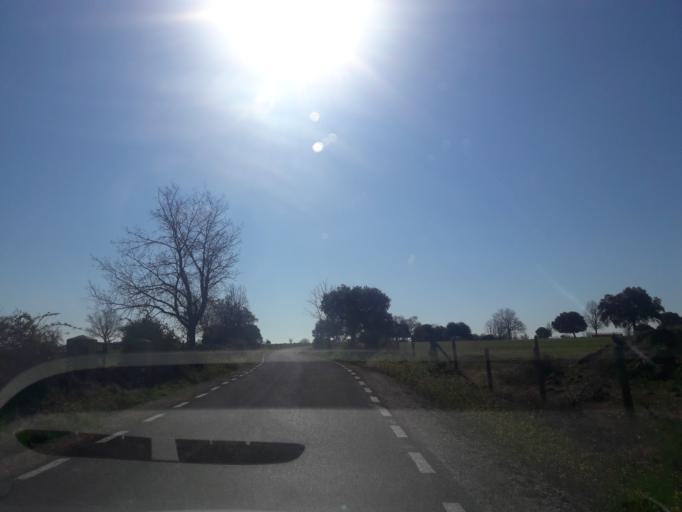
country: ES
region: Castille and Leon
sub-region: Provincia de Salamanca
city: Valsalabroso
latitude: 41.1734
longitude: -6.5090
